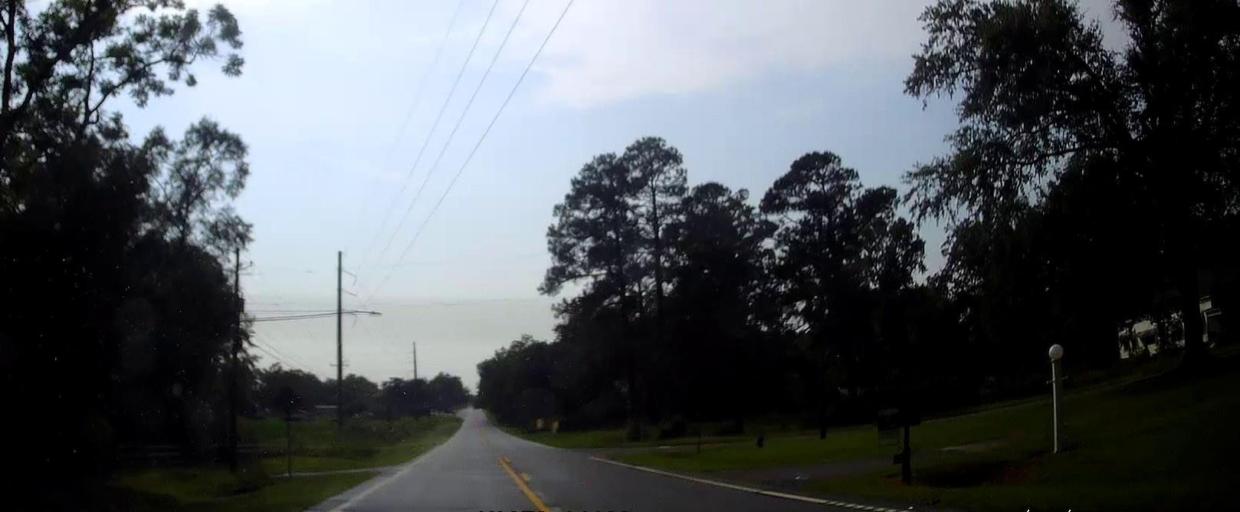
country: US
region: Georgia
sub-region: Twiggs County
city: Jeffersonville
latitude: 32.6021
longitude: -83.2445
